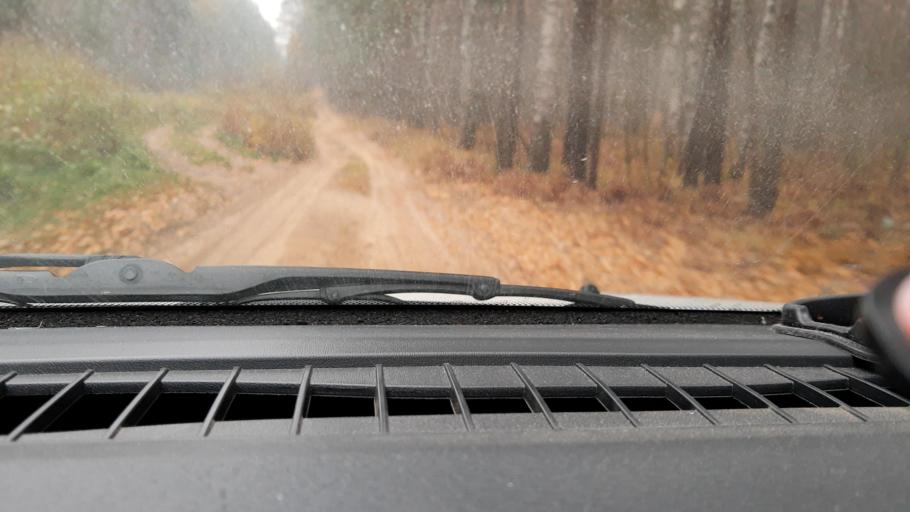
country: RU
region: Nizjnij Novgorod
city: Sitniki
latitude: 56.4322
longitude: 44.0630
